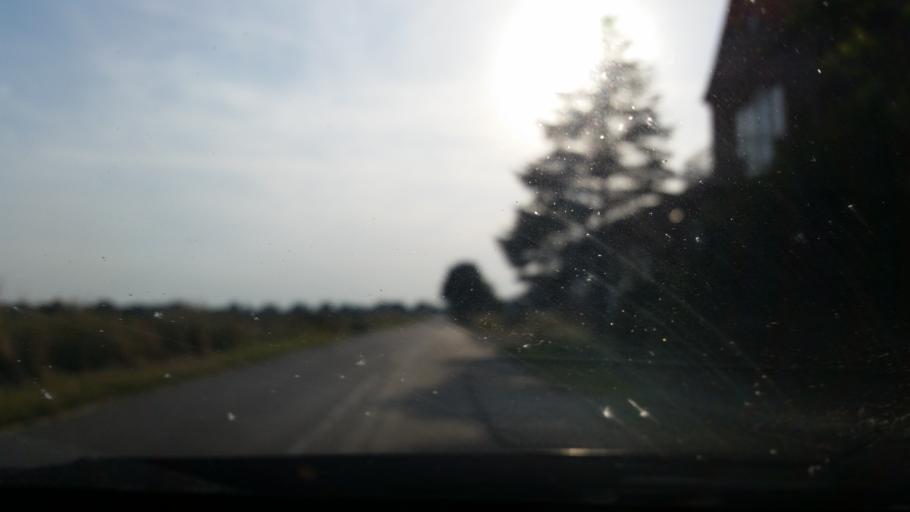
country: DK
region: Central Jutland
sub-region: Odder Kommune
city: Odder
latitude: 55.8910
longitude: 10.1836
